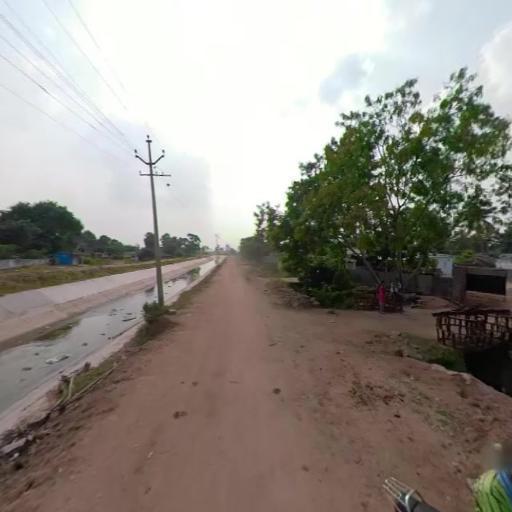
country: IN
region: Telangana
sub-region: Nalgonda
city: Suriapet
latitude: 17.2102
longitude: 79.5091
